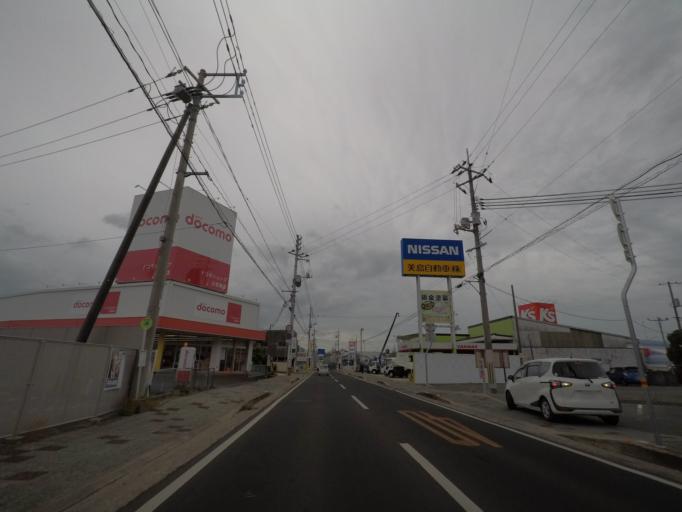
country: JP
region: Kagawa
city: Tonosho
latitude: 34.4888
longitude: 134.1943
